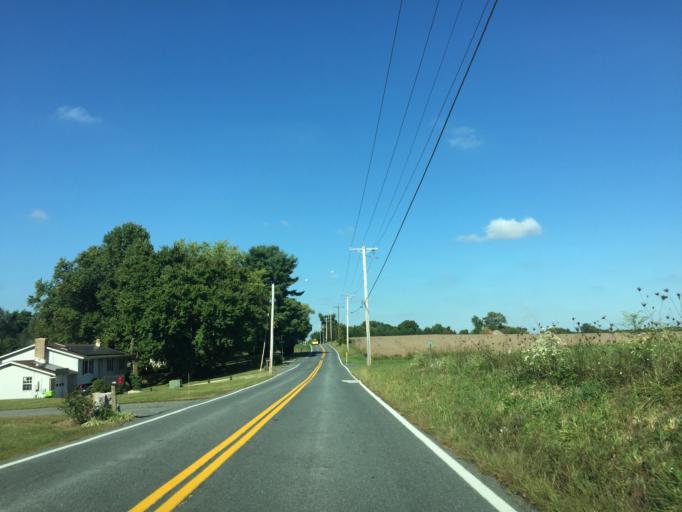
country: US
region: Maryland
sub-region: Harford County
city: Bel Air North
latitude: 39.5769
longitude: -76.4228
